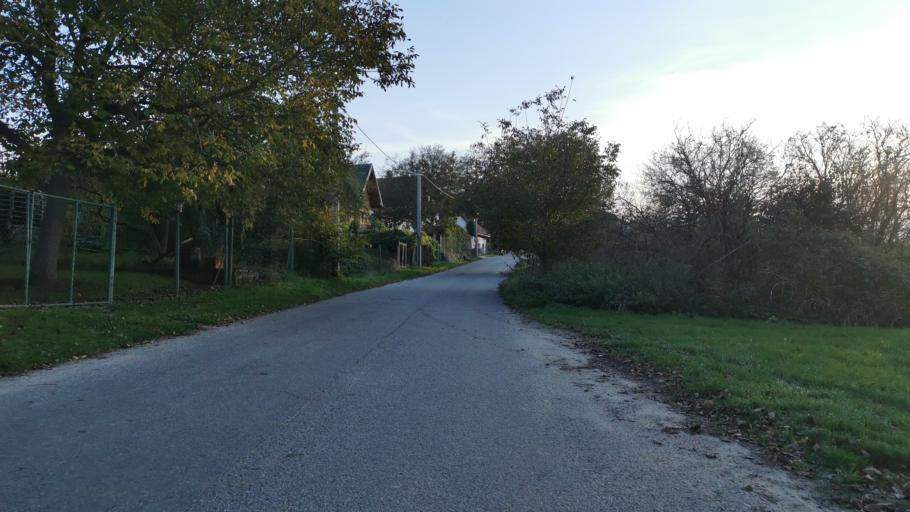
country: SK
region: Trnavsky
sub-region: Okres Skalica
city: Skalica
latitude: 48.8365
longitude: 17.2408
